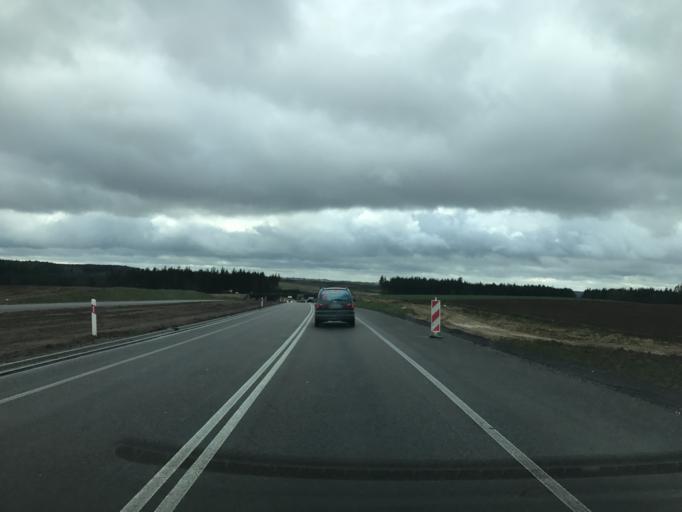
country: PL
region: Warmian-Masurian Voivodeship
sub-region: Powiat olsztynski
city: Olsztynek
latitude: 53.6194
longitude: 20.3364
